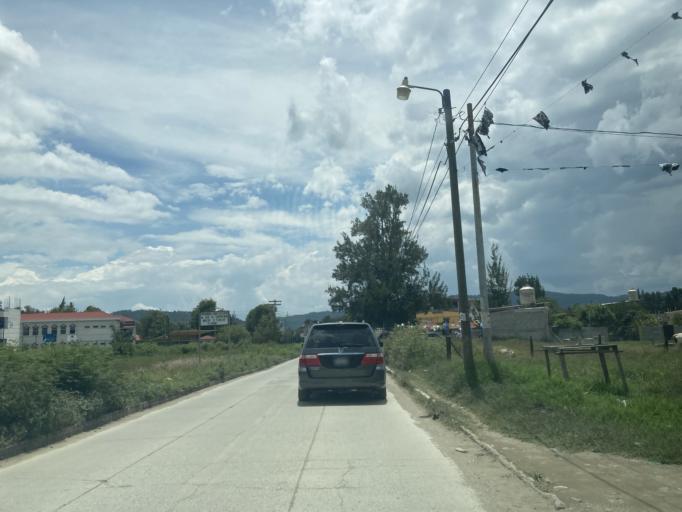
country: GT
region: Huehuetenango
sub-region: Municipio de Huehuetenango
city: Huehuetenango
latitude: 15.3236
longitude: -91.4955
